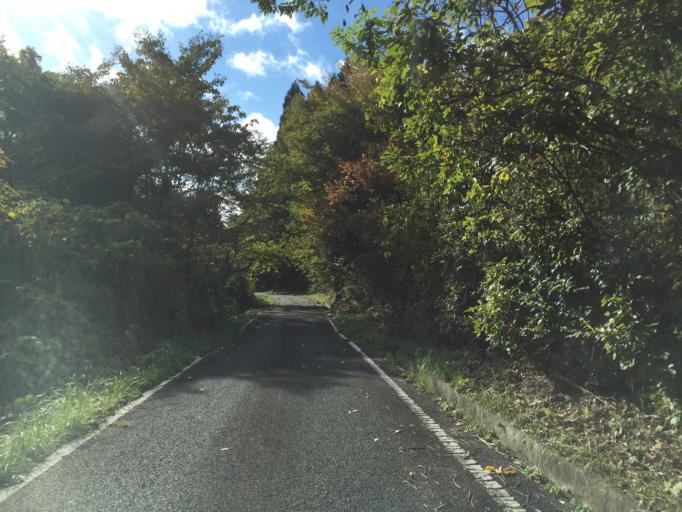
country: JP
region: Fukushima
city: Nihommatsu
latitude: 37.6765
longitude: 140.3784
